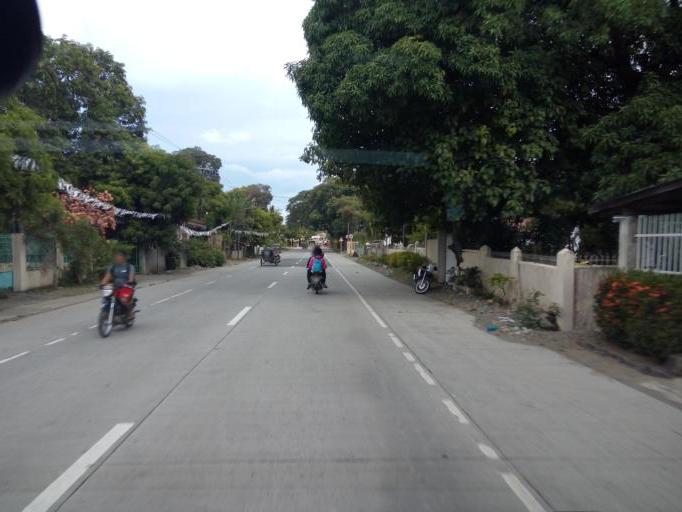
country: PH
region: Central Luzon
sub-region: Province of Nueva Ecija
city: Parista
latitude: 15.8337
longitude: 120.9439
